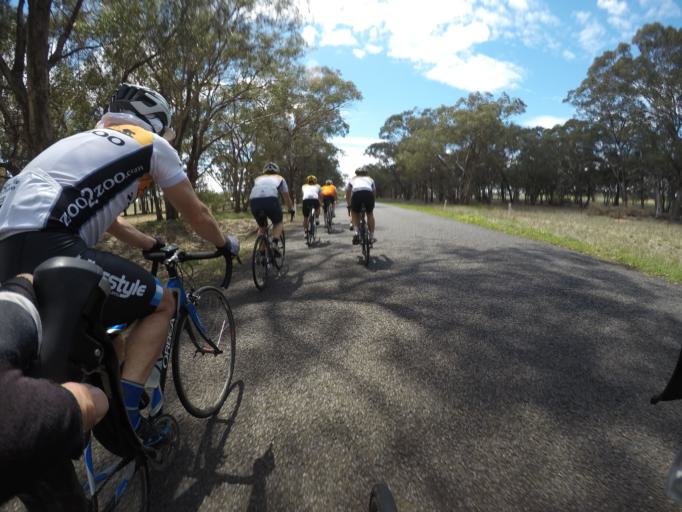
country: AU
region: New South Wales
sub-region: Dubbo Municipality
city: Dubbo
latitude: -32.3503
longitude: 148.5949
